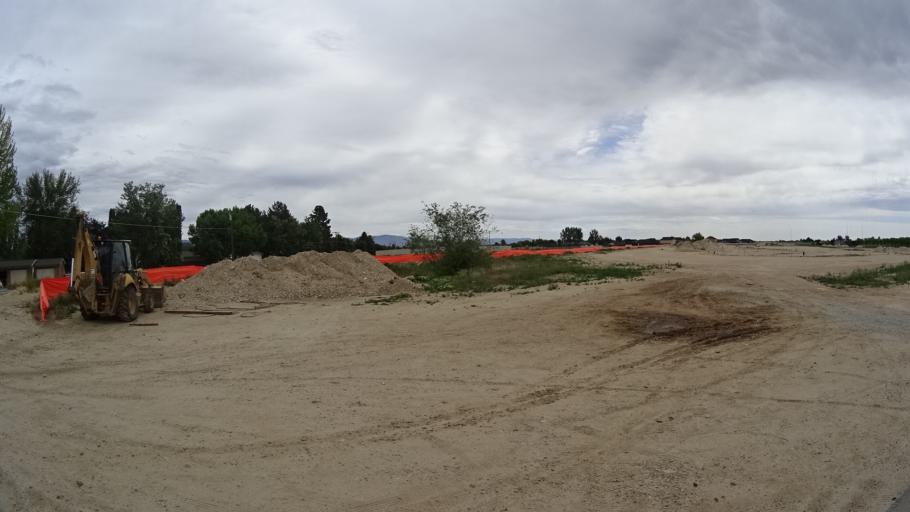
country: US
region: Idaho
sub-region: Ada County
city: Meridian
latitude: 43.5752
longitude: -116.4137
